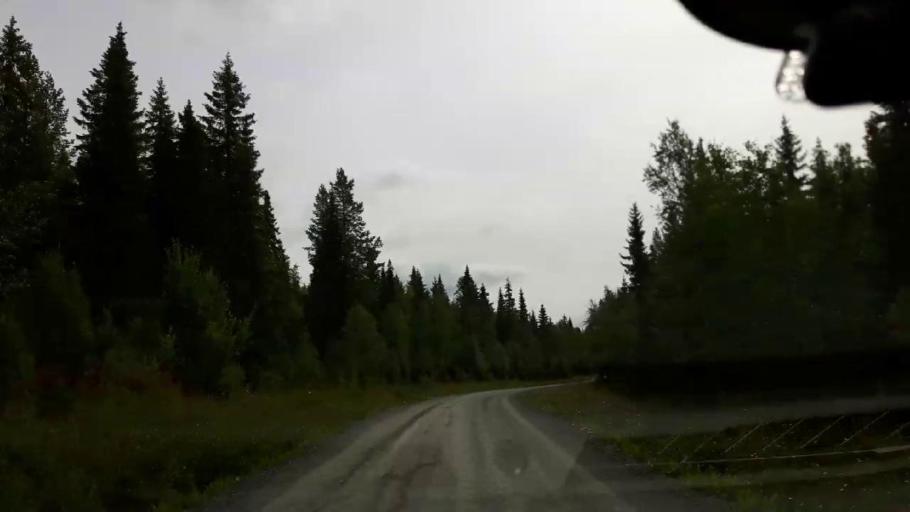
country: SE
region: Jaemtland
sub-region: Krokoms Kommun
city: Valla
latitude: 63.6366
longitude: 14.0158
